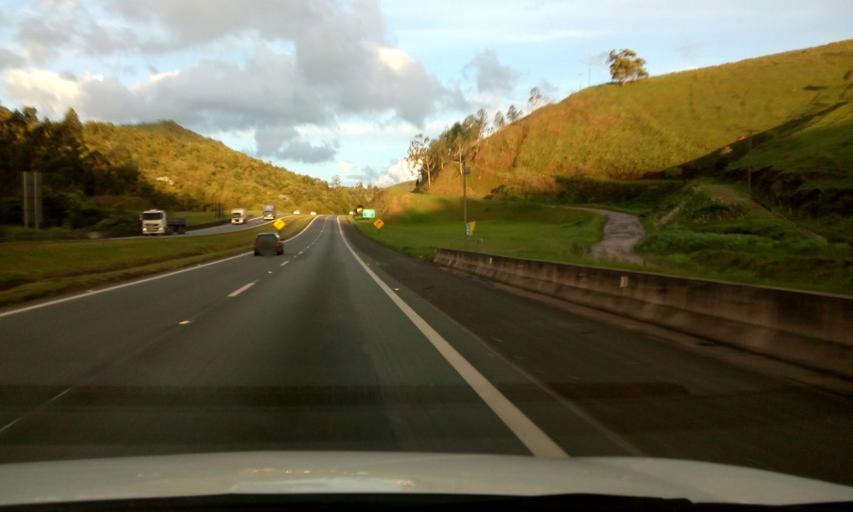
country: BR
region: Sao Paulo
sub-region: Piracaia
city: Piracaia
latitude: -23.1730
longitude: -46.2751
